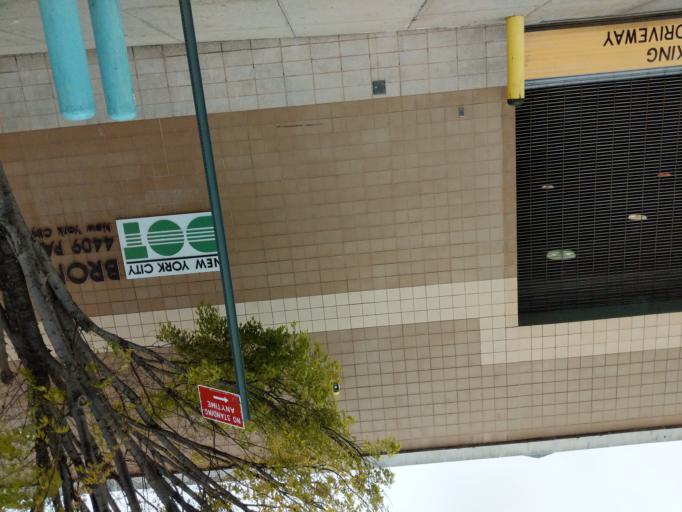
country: US
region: New York
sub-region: Bronx
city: The Bronx
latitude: 40.8526
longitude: -73.8968
